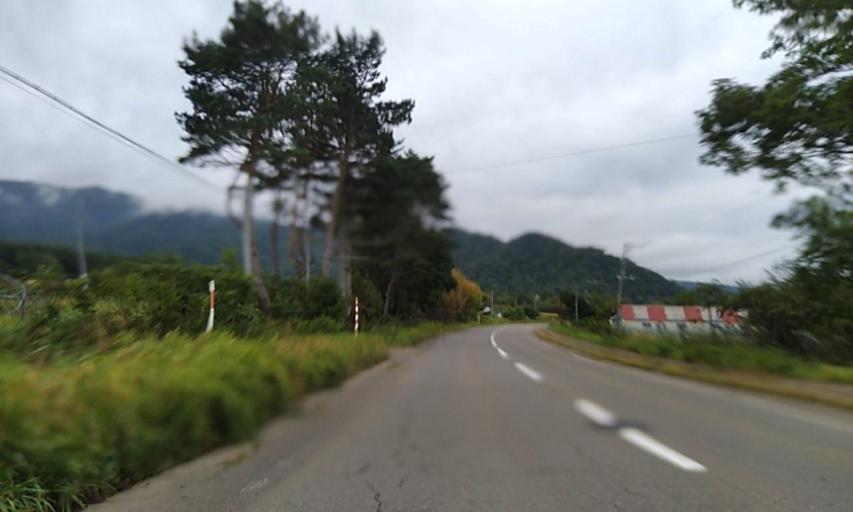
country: JP
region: Hokkaido
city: Bihoro
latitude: 43.5813
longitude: 144.2768
